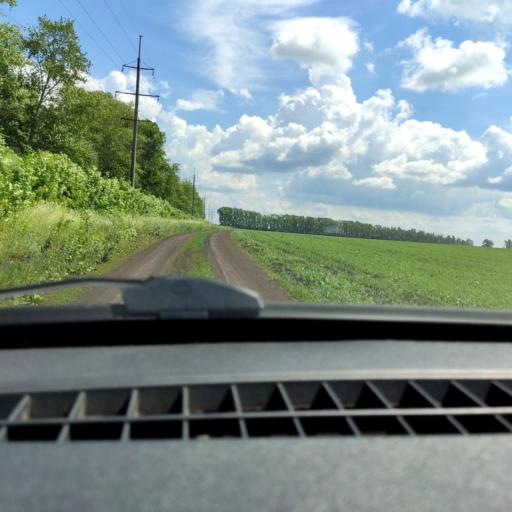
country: RU
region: Bashkortostan
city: Kabakovo
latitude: 54.5211
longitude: 56.0739
